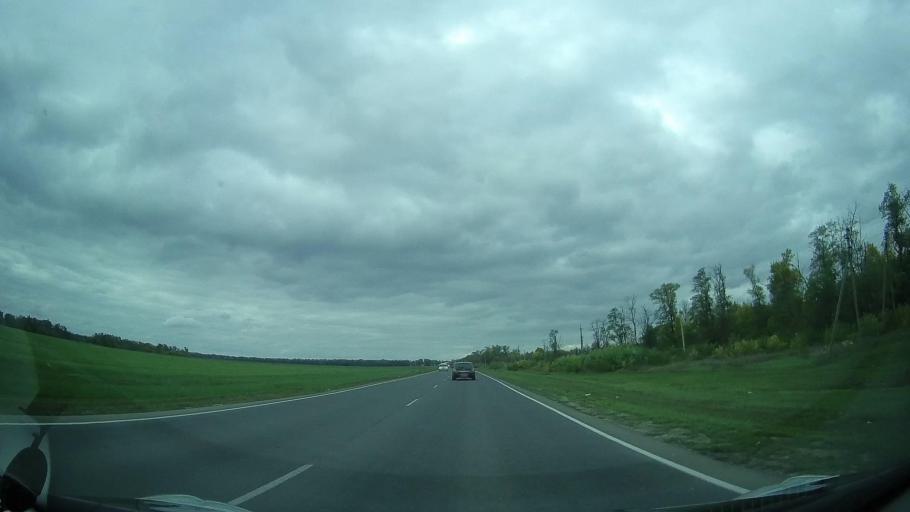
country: RU
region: Rostov
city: Yegorlykskaya
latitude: 46.5769
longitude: 40.6321
